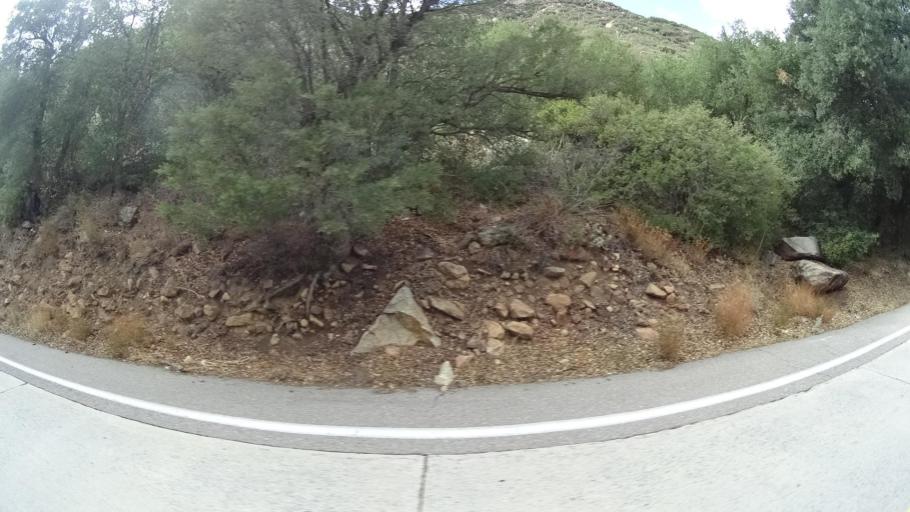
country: US
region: California
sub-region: San Diego County
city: Pine Valley
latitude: 32.7899
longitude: -116.4970
